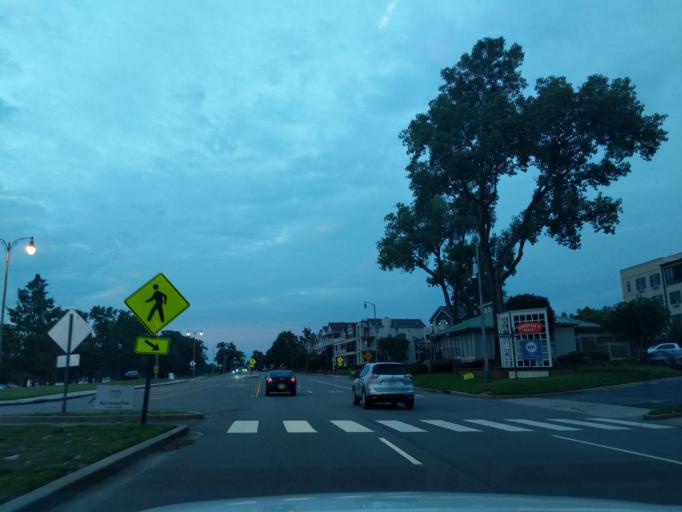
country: US
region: Tennessee
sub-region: Shelby County
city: Memphis
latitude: 35.1607
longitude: -90.0558
